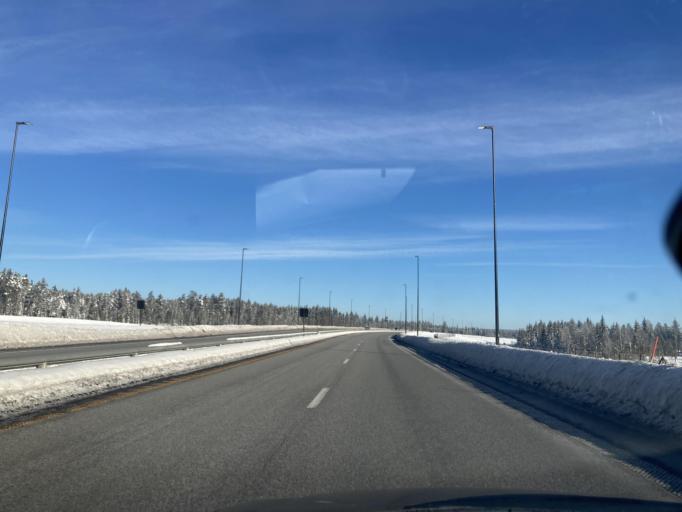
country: NO
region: Hedmark
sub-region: Loten
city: Loten
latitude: 60.8723
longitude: 11.4434
